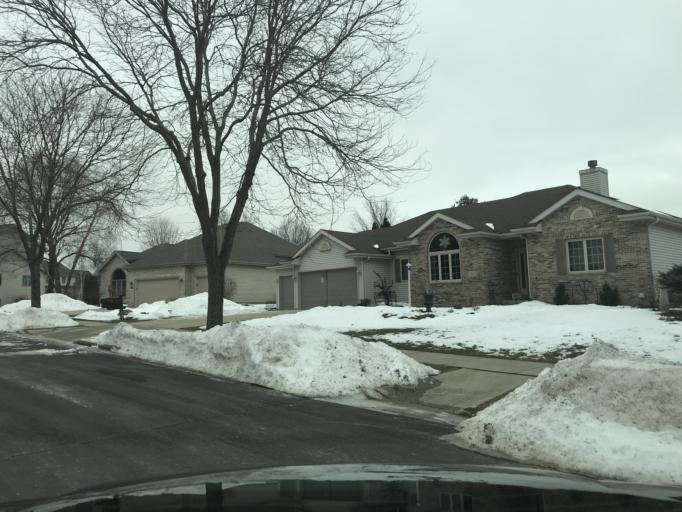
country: US
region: Wisconsin
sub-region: Dane County
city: Monona
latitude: 43.0804
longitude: -89.2740
